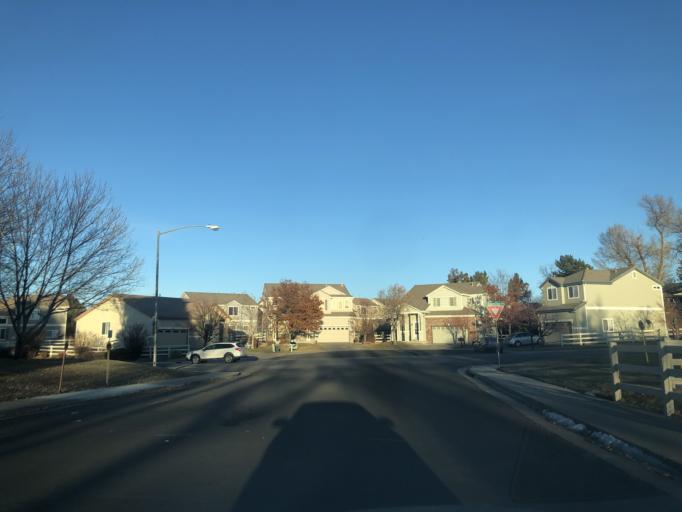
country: US
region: Colorado
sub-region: Adams County
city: Aurora
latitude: 39.7151
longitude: -104.8146
